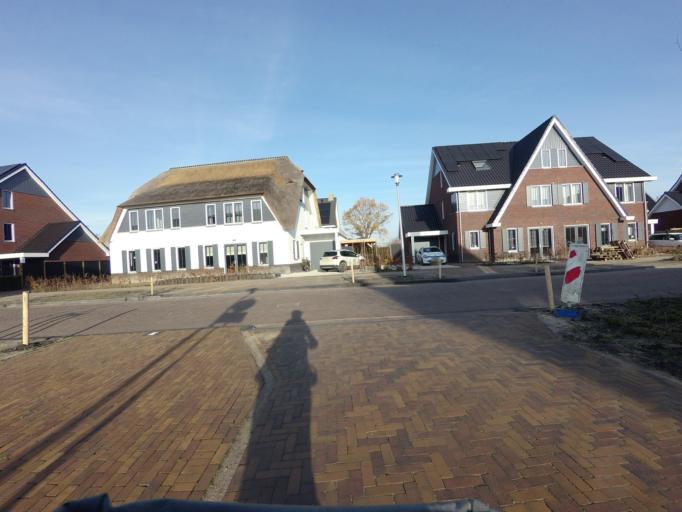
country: NL
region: Utrecht
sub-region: Stichtse Vecht
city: Spechtenkamp
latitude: 52.1143
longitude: 5.0112
